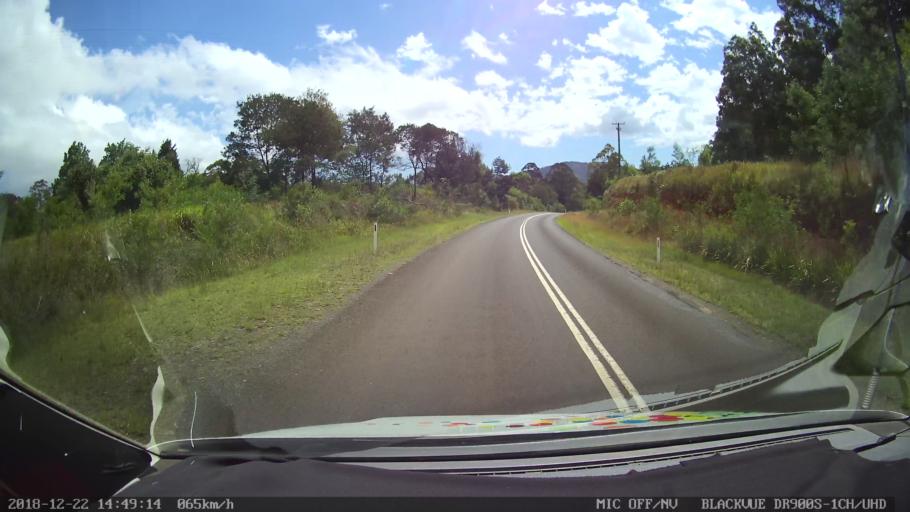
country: AU
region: New South Wales
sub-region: Bellingen
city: Dorrigo
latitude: -30.1877
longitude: 152.5499
